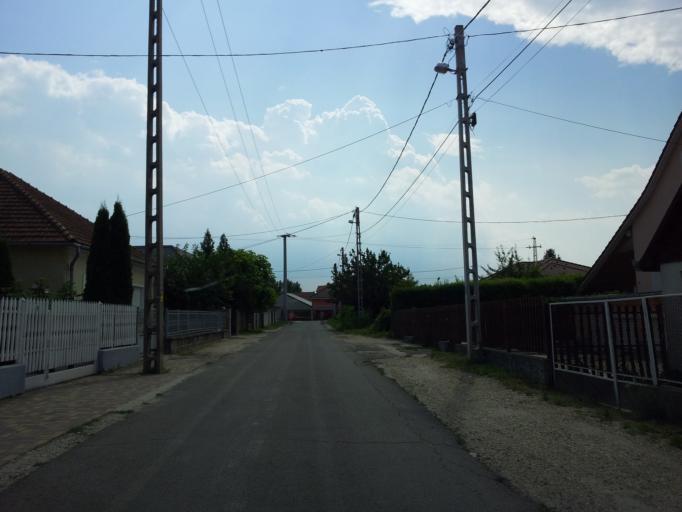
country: HU
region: Pest
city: Toekoel
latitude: 47.3140
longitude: 18.9691
